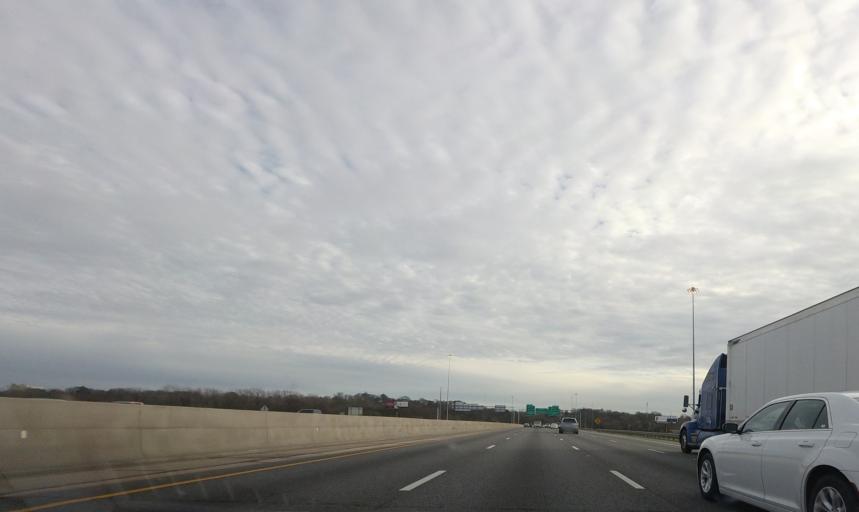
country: US
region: Alabama
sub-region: Jefferson County
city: Birmingham
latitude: 33.5410
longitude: -86.8257
